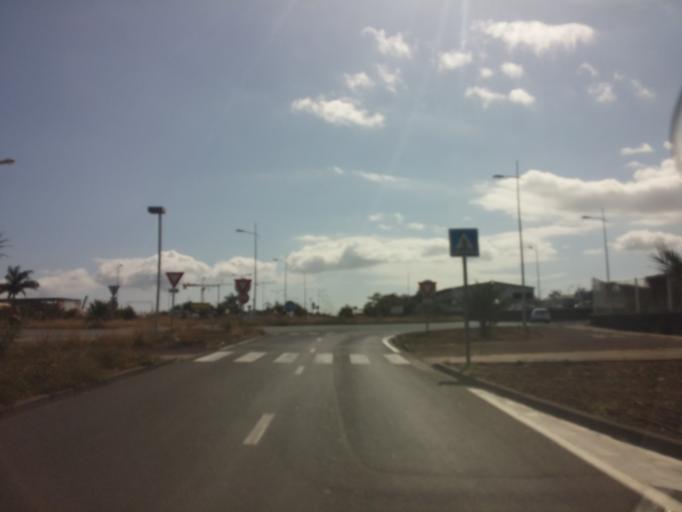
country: RE
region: Reunion
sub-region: Reunion
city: Le Port
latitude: -20.9660
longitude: 55.2949
